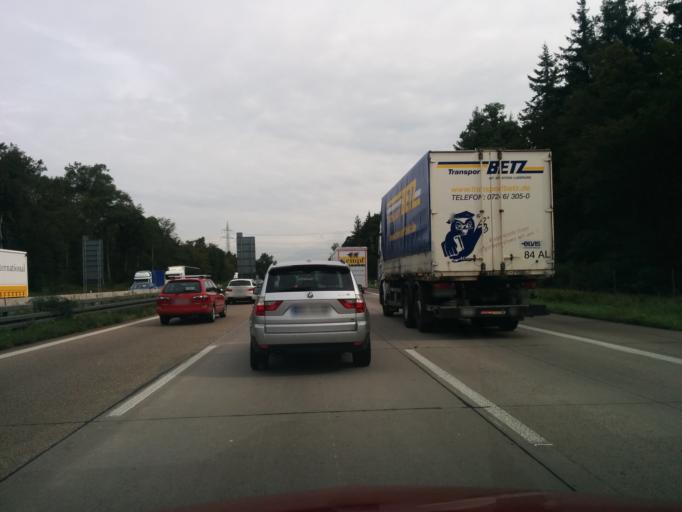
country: DE
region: Baden-Wuerttemberg
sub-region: Karlsruhe Region
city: Forst
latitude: 49.1741
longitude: 8.5758
